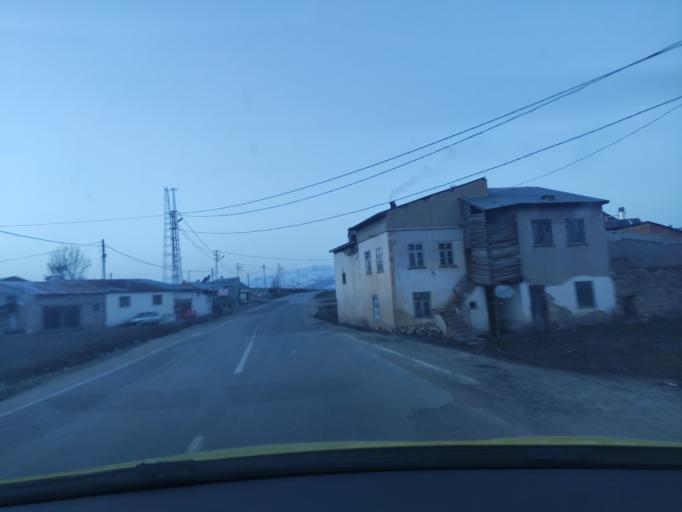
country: TR
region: Bayburt
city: Aydintepe
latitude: 40.3362
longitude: 40.1261
